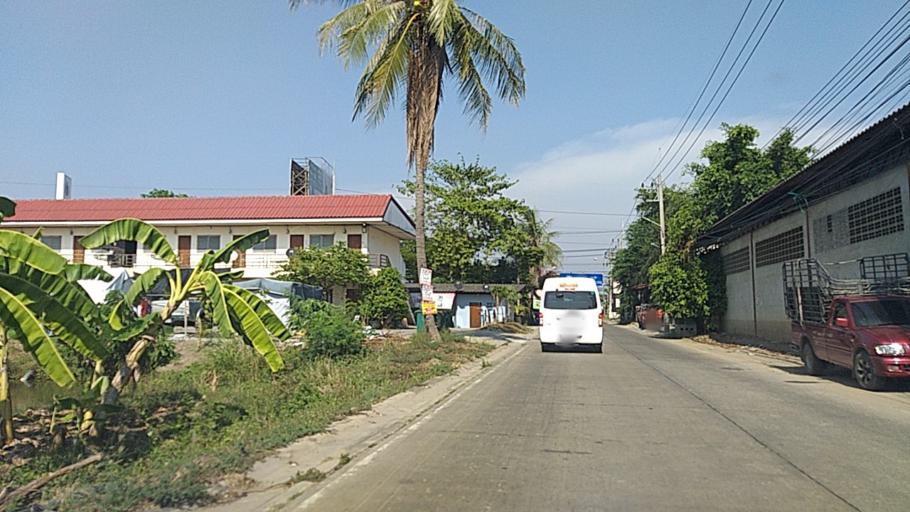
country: TH
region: Nakhon Pathom
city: Salaya
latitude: 13.8250
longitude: 100.3136
